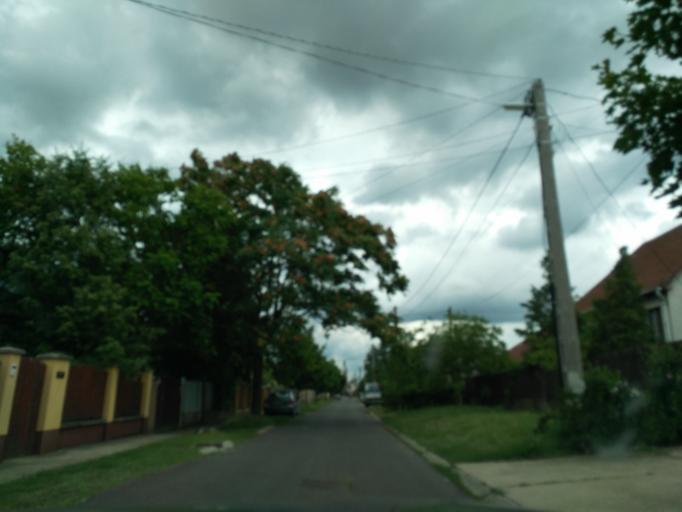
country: HU
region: Hajdu-Bihar
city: Debrecen
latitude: 47.5449
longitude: 21.6562
